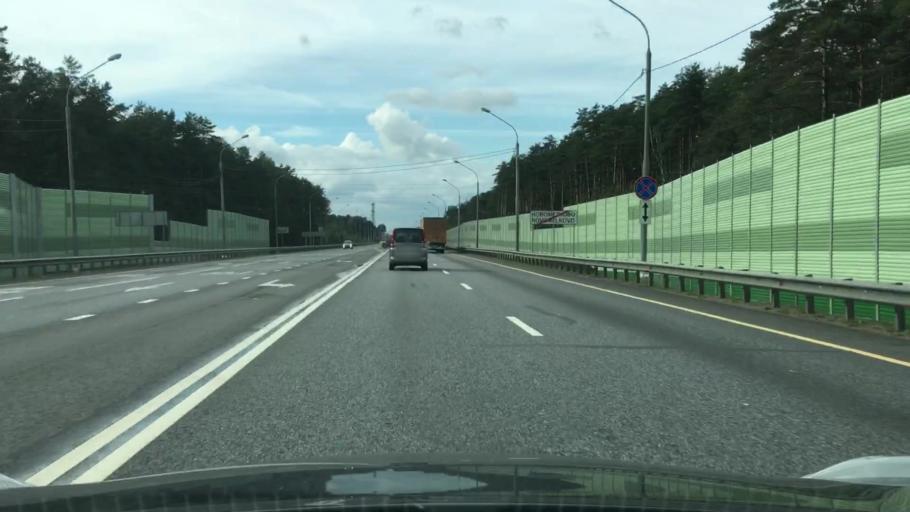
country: RU
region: Tverskaya
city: Radchenko
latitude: 56.6801
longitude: 36.3896
